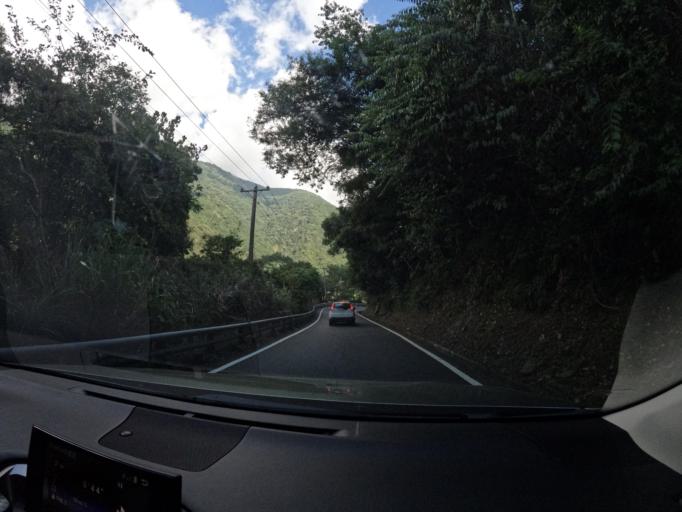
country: TW
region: Taiwan
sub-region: Taitung
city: Taitung
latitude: 23.1791
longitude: 121.0428
